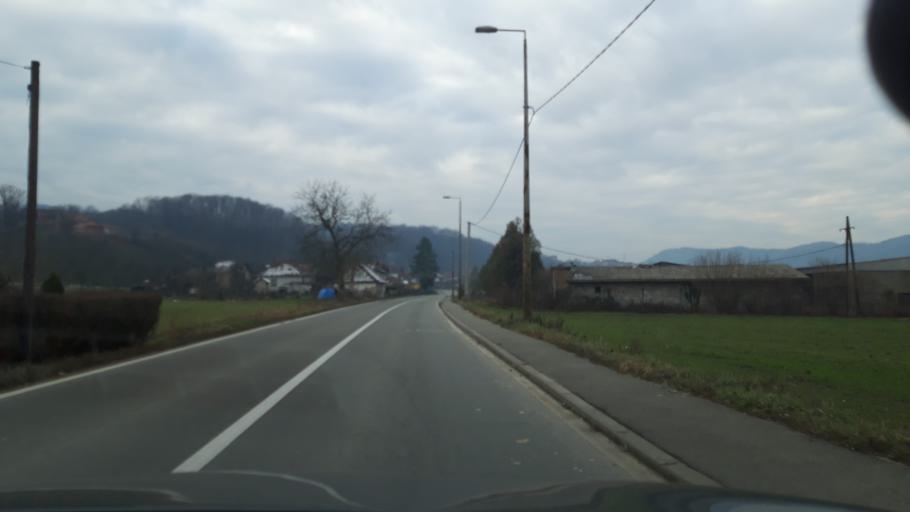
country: BA
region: Republika Srpska
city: Zvornik
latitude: 44.4098
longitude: 19.1456
